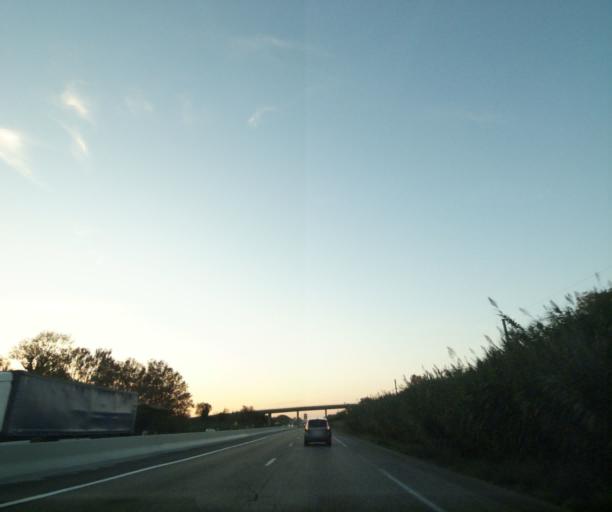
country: FR
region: Provence-Alpes-Cote d'Azur
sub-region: Departement des Bouches-du-Rhone
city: Fontvieille
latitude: 43.6418
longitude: 4.7141
